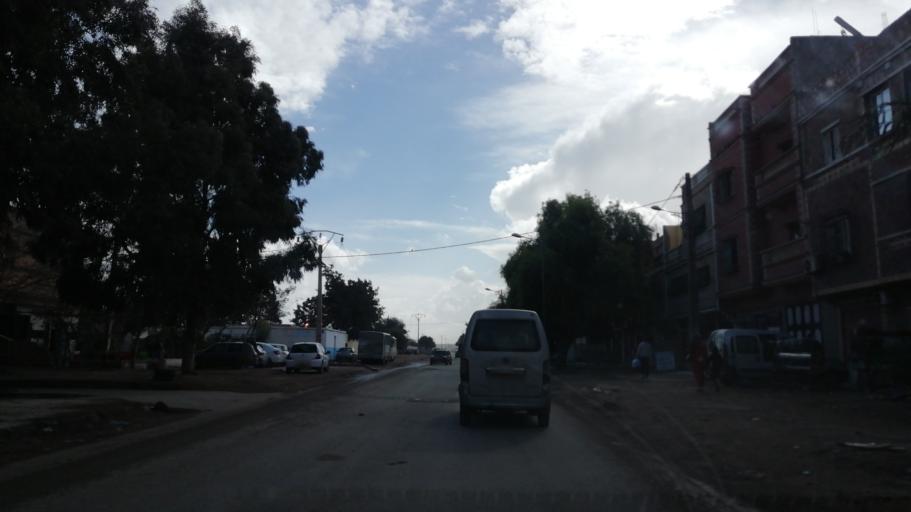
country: DZ
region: Oran
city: Sidi ech Chahmi
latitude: 35.6509
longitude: -0.5657
